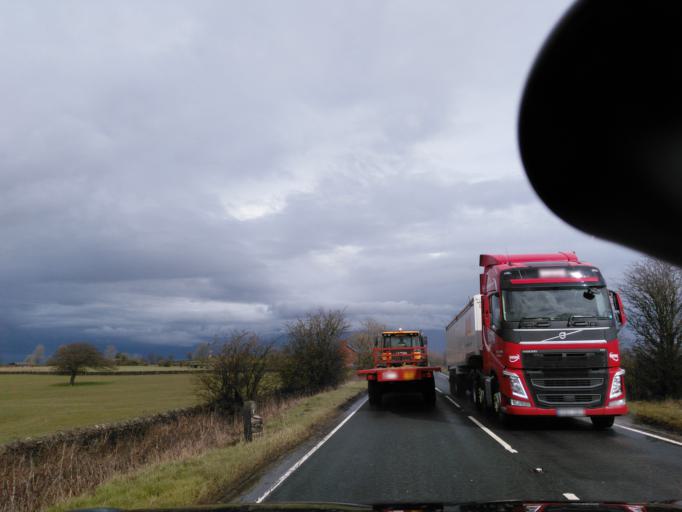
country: GB
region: England
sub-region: North Yorkshire
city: Stainburn
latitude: 54.0061
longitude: -1.6109
